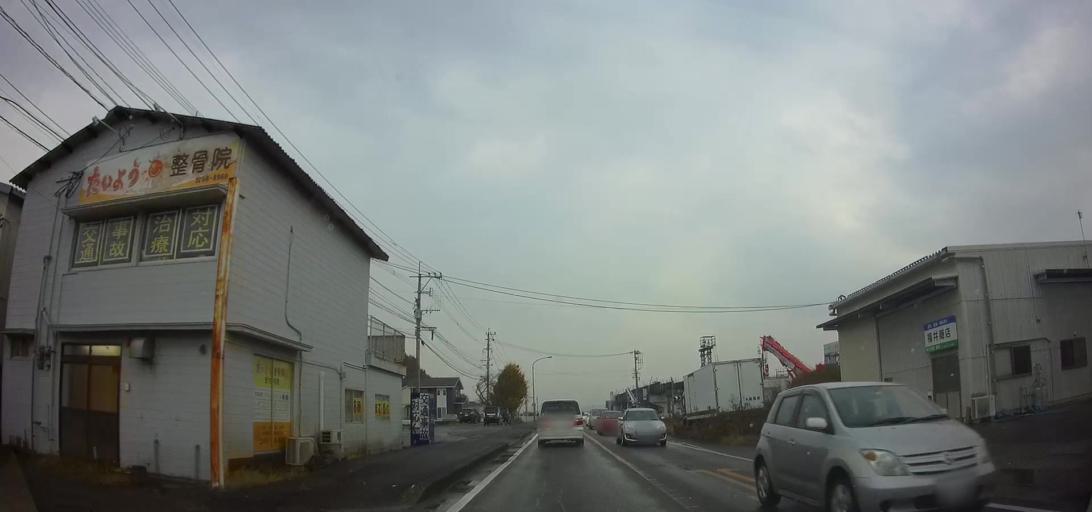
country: JP
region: Nagasaki
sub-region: Isahaya-shi
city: Isahaya
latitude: 32.8361
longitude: 130.1078
